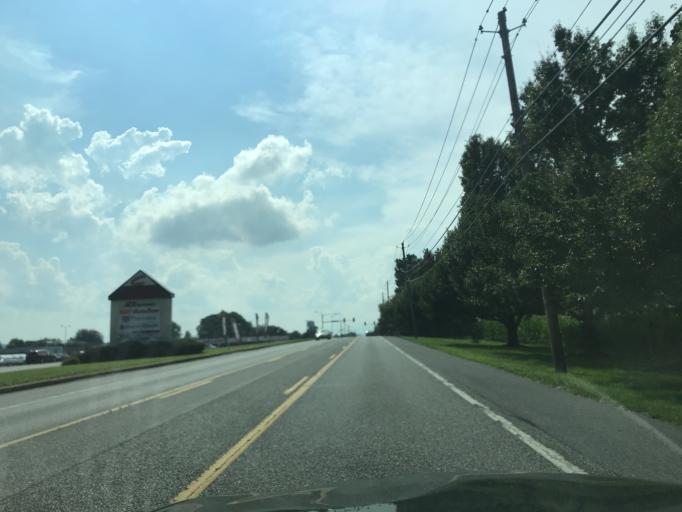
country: US
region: Pennsylvania
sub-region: Lancaster County
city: Columbia
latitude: 40.0319
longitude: -76.4748
